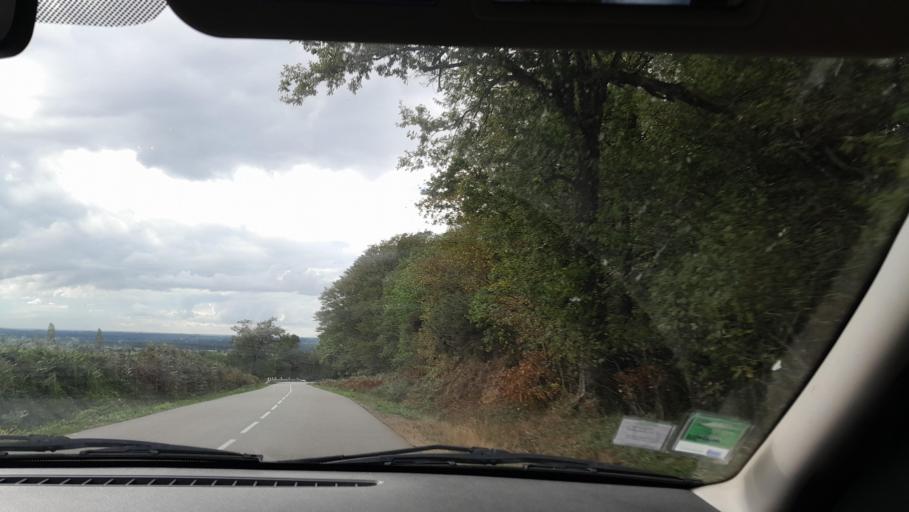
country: FR
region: Brittany
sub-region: Departement d'Ille-et-Vilaine
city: Le Pertre
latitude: 48.0444
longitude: -1.0790
